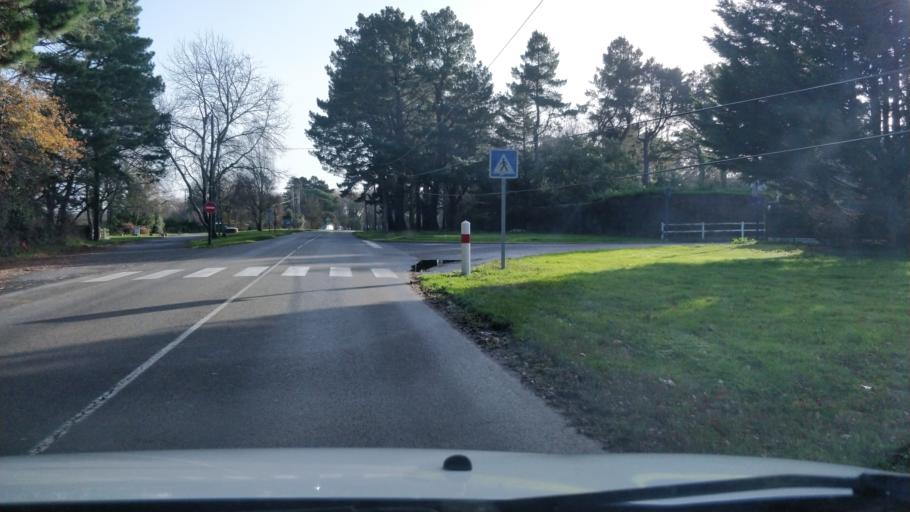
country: FR
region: Pays de la Loire
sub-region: Departement de la Loire-Atlantique
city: Mesquer
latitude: 47.3965
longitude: -2.4700
